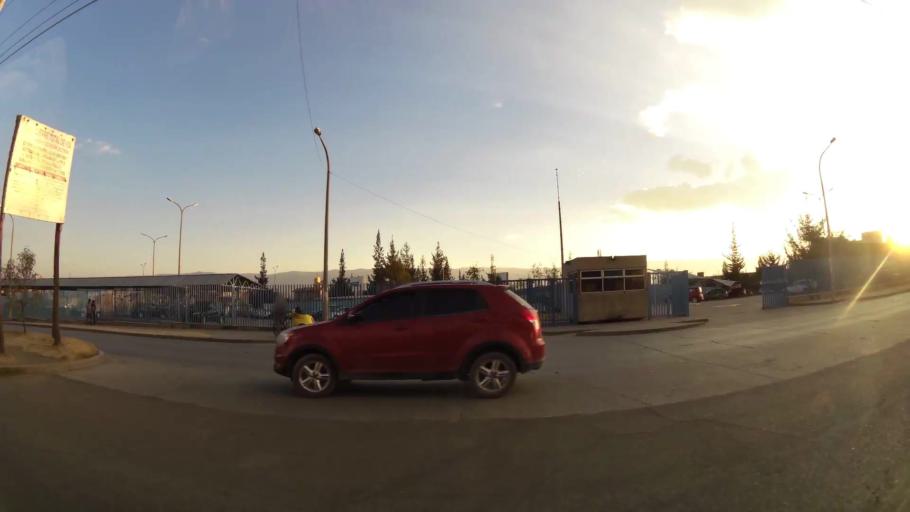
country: PE
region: Junin
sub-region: Provincia de Huancayo
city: El Tambo
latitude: -12.0522
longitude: -75.2267
